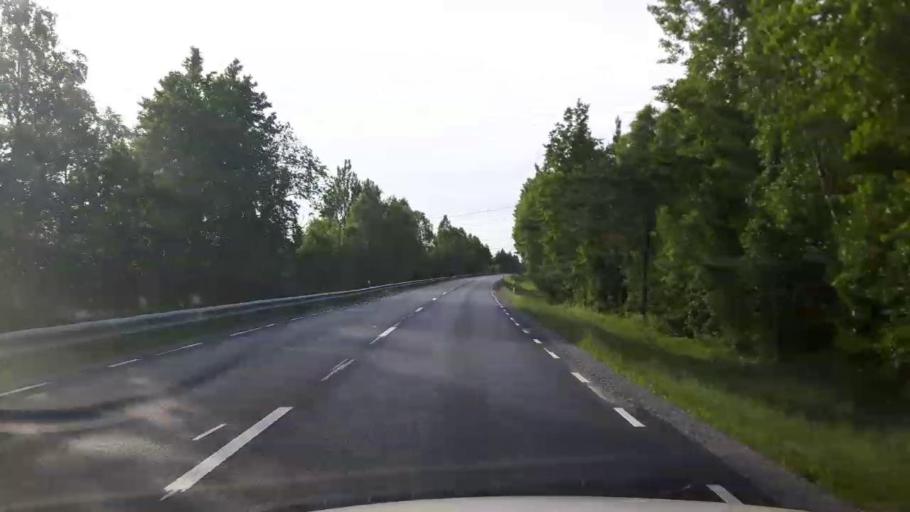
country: SE
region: Uppsala
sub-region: Habo Kommun
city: Balsta
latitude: 59.6367
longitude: 17.5788
